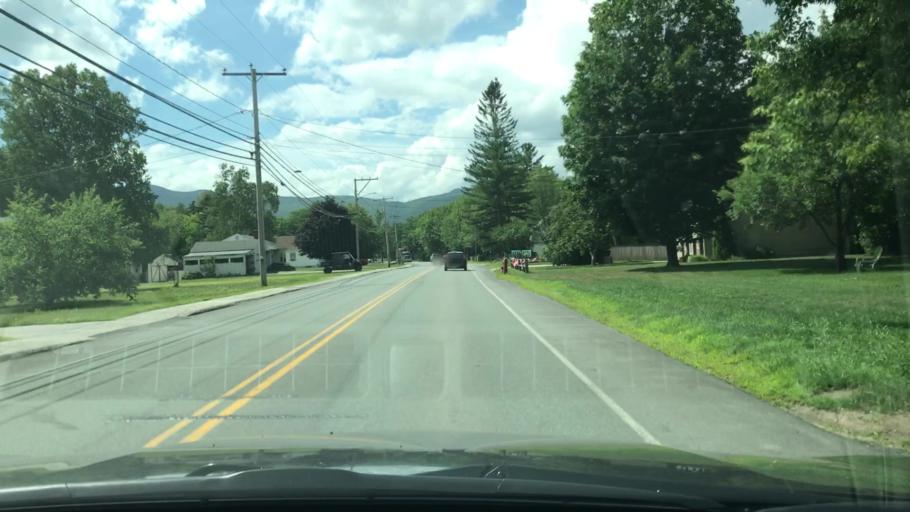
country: US
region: New Hampshire
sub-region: Coos County
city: Gorham
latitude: 44.3987
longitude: -71.2060
